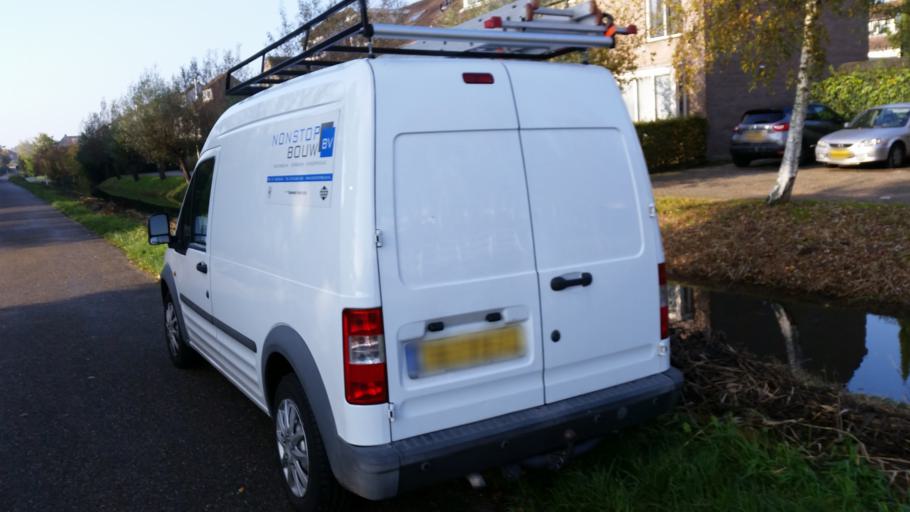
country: NL
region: North Holland
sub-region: Gemeente Ouder-Amstel
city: Ouderkerk aan de Amstel
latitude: 52.2938
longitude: 4.9218
